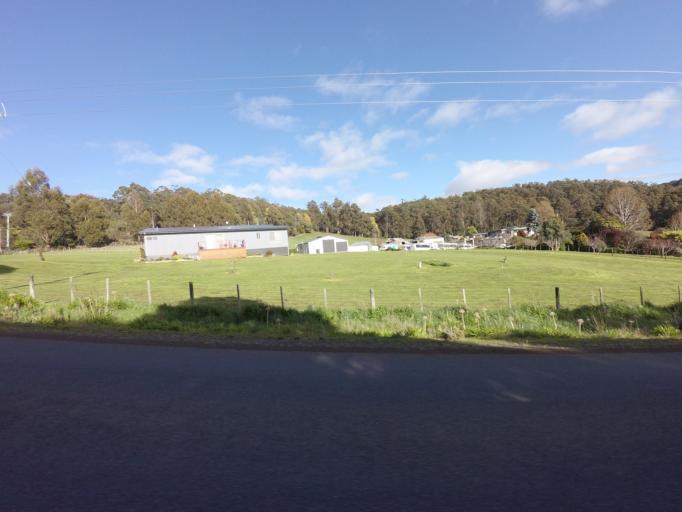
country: AU
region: Tasmania
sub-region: Huon Valley
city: Geeveston
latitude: -43.1963
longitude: 146.9569
